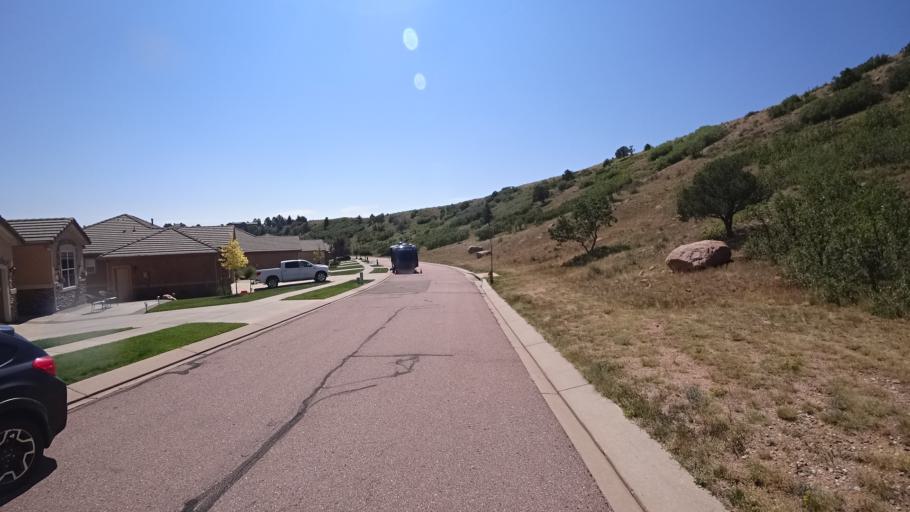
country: US
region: Colorado
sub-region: El Paso County
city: Air Force Academy
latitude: 38.9403
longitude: -104.8729
